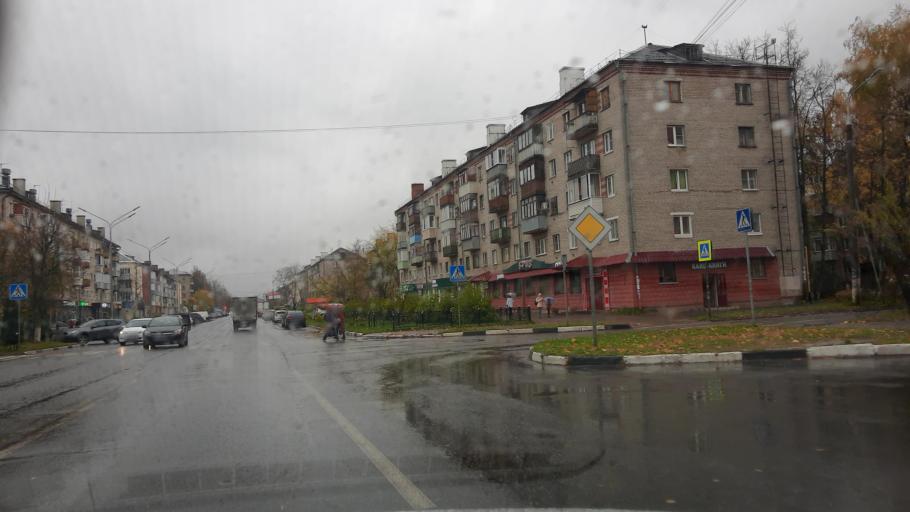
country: RU
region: Moskovskaya
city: Elektrostal'
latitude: 55.8008
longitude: 38.4376
